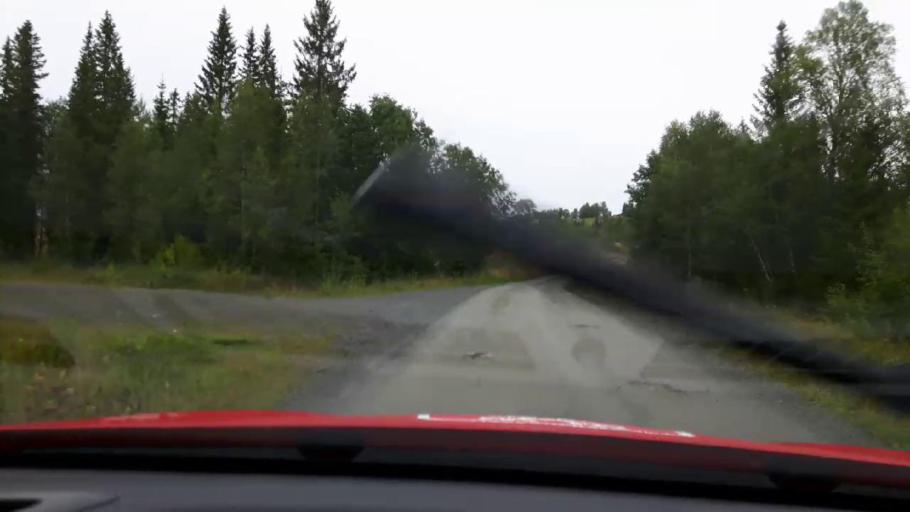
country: SE
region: Jaemtland
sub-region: Are Kommun
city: Are
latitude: 63.5087
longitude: 12.7121
